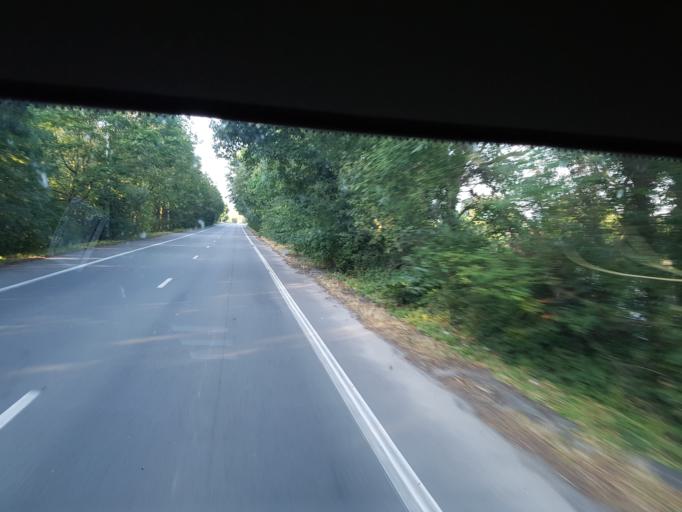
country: BE
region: Wallonia
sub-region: Province du Hainaut
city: Antoing
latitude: 50.5562
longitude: 3.4476
